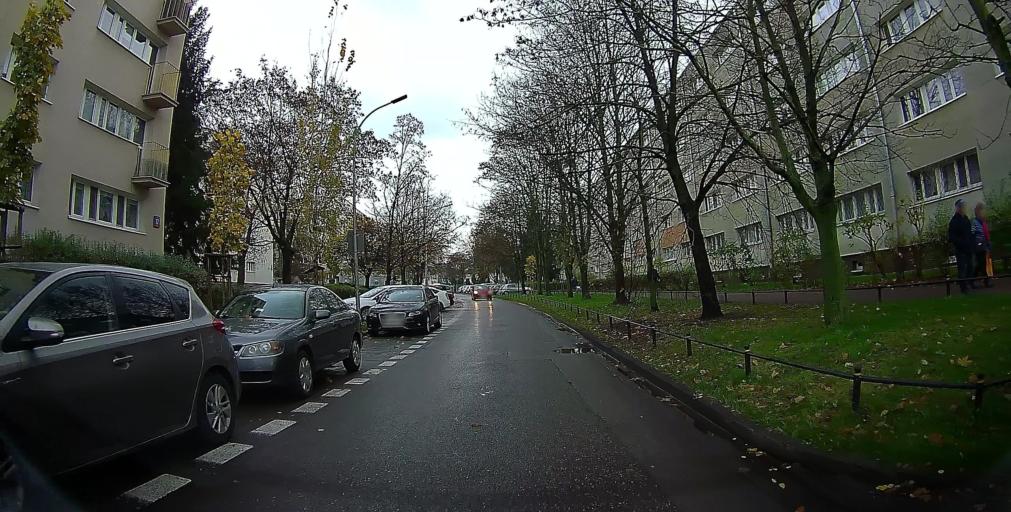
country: PL
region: Masovian Voivodeship
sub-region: Warszawa
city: Ochota
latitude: 52.1970
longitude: 20.9790
